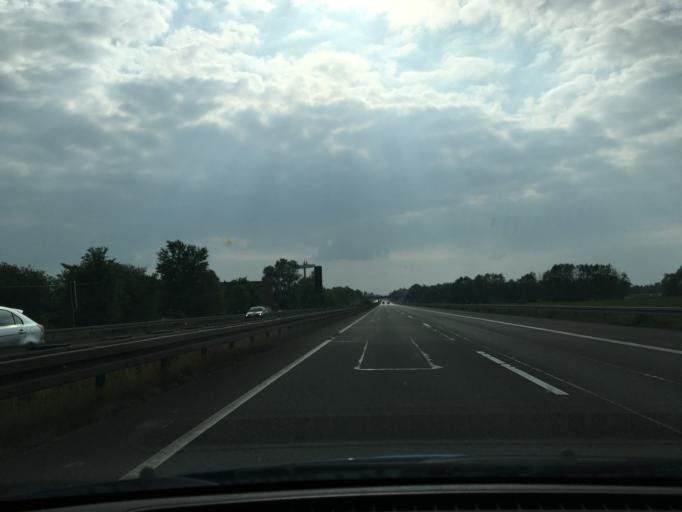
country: DE
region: Lower Saxony
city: Melle
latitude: 52.1956
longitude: 8.3697
